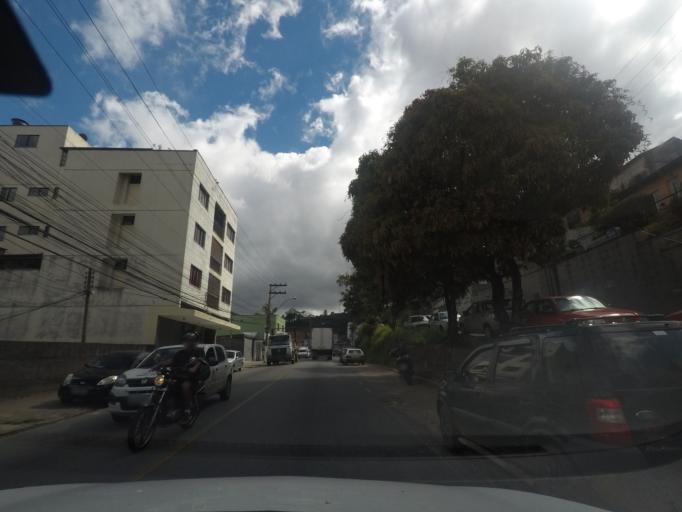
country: BR
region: Rio de Janeiro
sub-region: Teresopolis
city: Teresopolis
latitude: -22.4012
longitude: -42.9635
